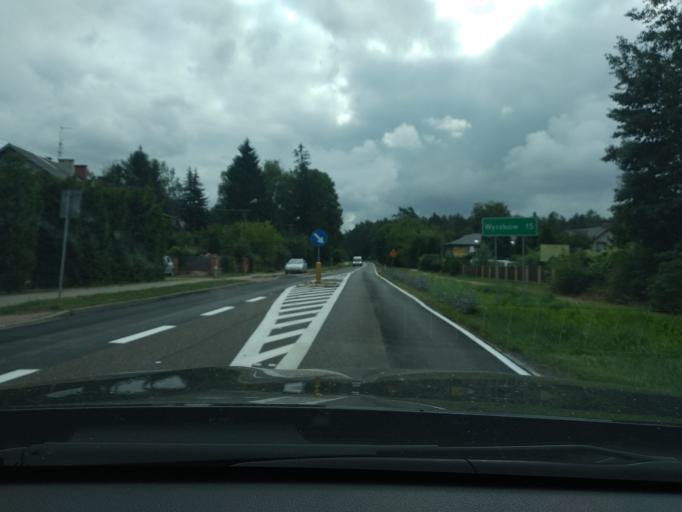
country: PL
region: Masovian Voivodeship
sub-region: Powiat pultuski
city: Obryte
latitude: 52.6469
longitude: 21.2530
